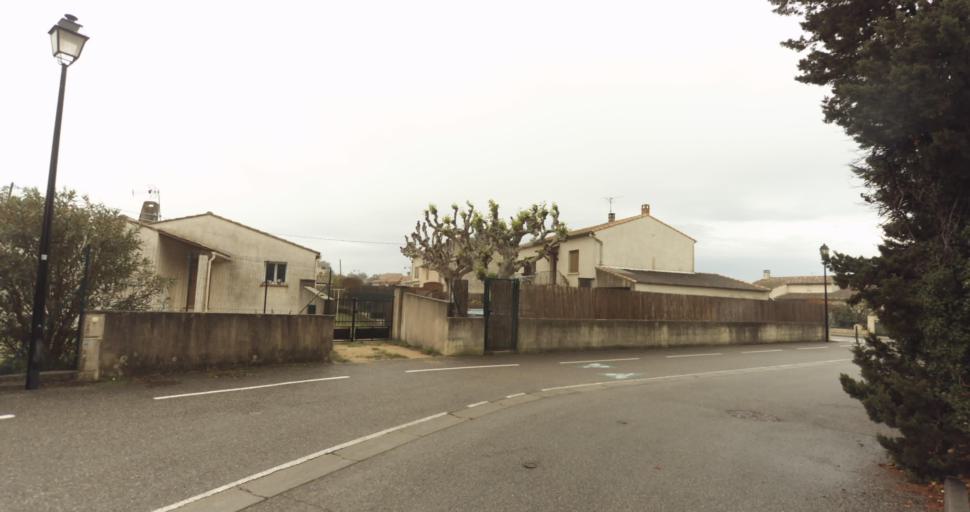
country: FR
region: Provence-Alpes-Cote d'Azur
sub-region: Departement des Bouches-du-Rhone
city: Rognonas
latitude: 43.9034
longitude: 4.8103
